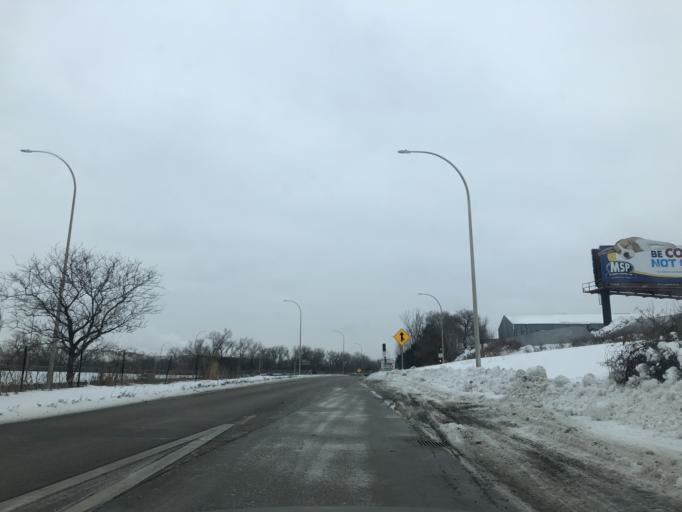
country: US
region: Minnesota
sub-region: Anoka County
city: Columbia Heights
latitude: 45.0429
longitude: -93.2853
